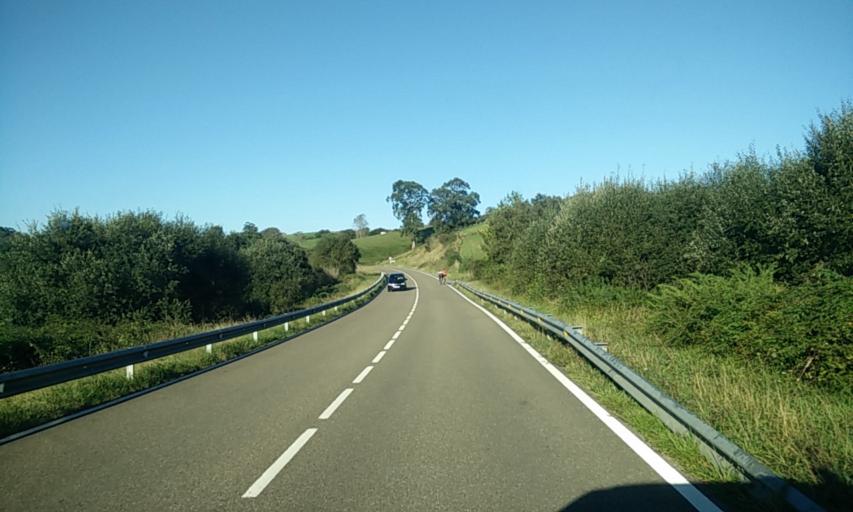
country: ES
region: Cantabria
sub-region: Provincia de Cantabria
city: Comillas
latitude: 43.3838
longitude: -4.3421
